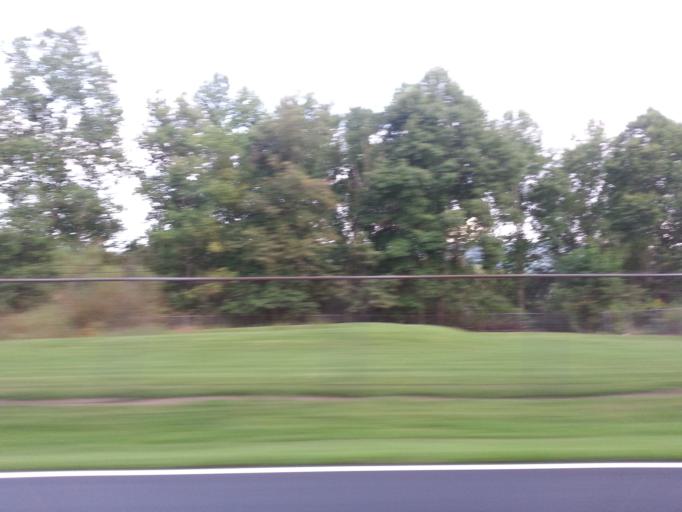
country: US
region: Tennessee
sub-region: Carter County
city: Hunter
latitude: 36.4504
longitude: -82.0410
